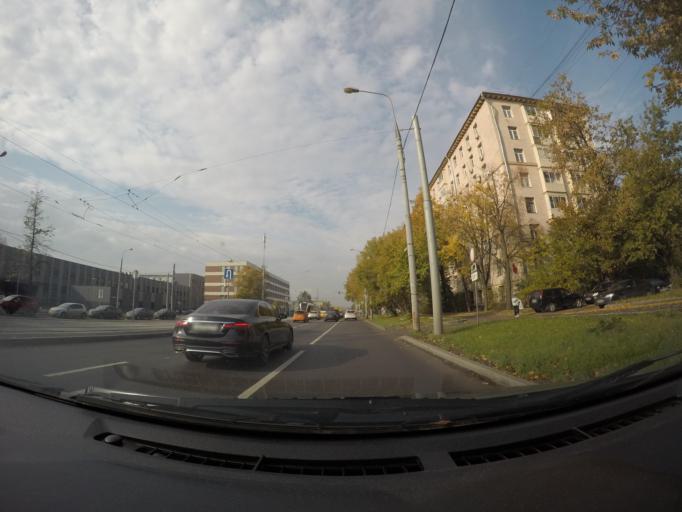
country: RU
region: Moscow
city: Lefortovo
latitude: 55.7694
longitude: 37.7290
